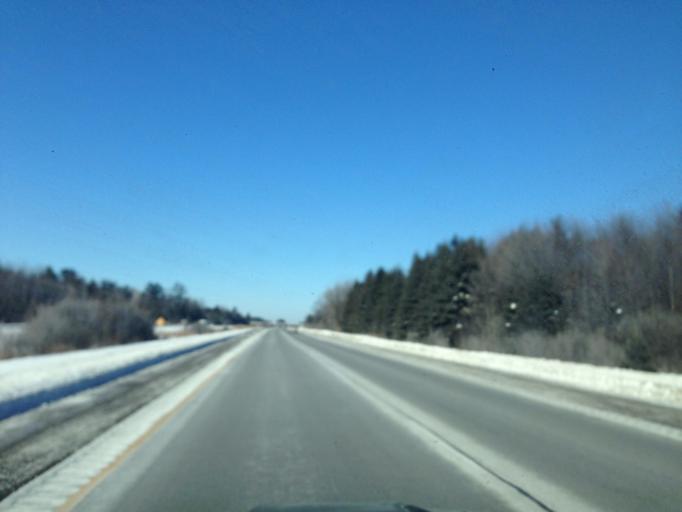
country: CA
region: Ontario
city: Ottawa
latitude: 45.3668
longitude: -75.5237
